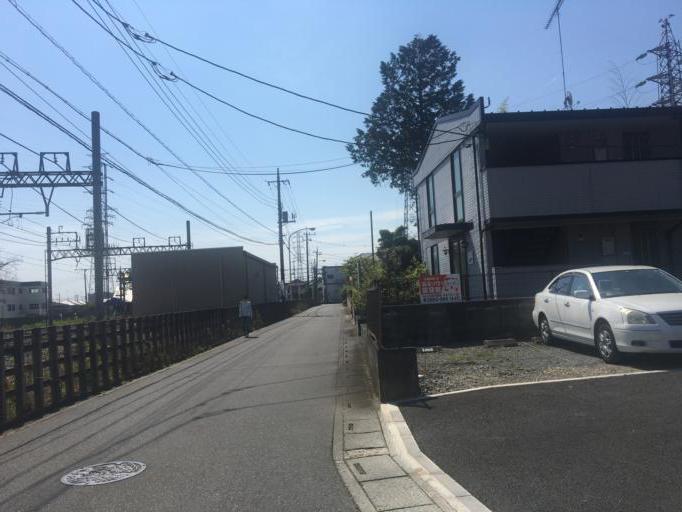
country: JP
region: Saitama
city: Ogawa
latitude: 36.0451
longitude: 139.3260
